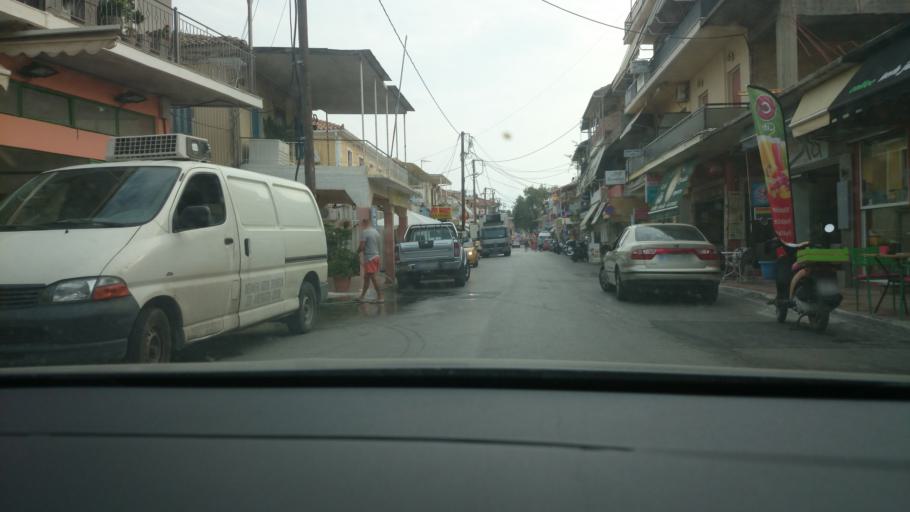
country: GR
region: Ionian Islands
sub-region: Lefkada
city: Nidri
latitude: 38.7075
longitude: 20.7104
